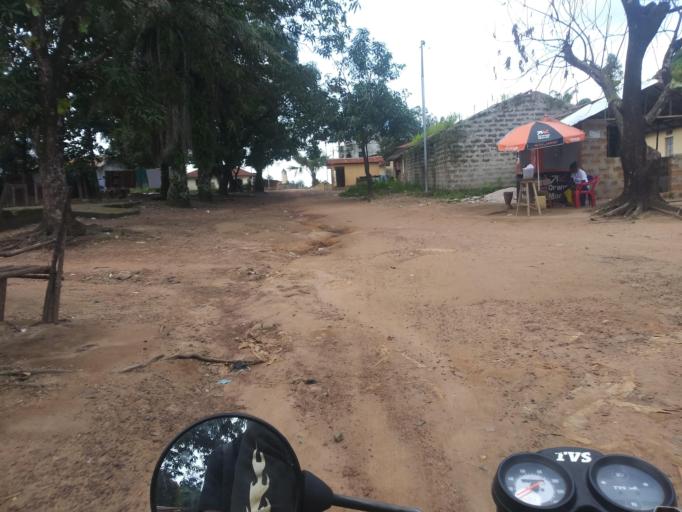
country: SL
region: Northern Province
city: Makeni
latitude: 8.8738
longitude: -12.0410
